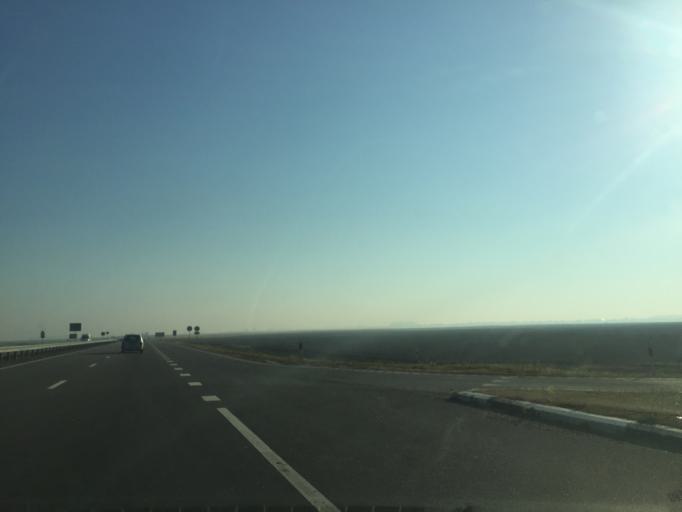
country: BY
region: Gomel
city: Kastsyukowka
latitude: 52.4862
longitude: 30.7815
